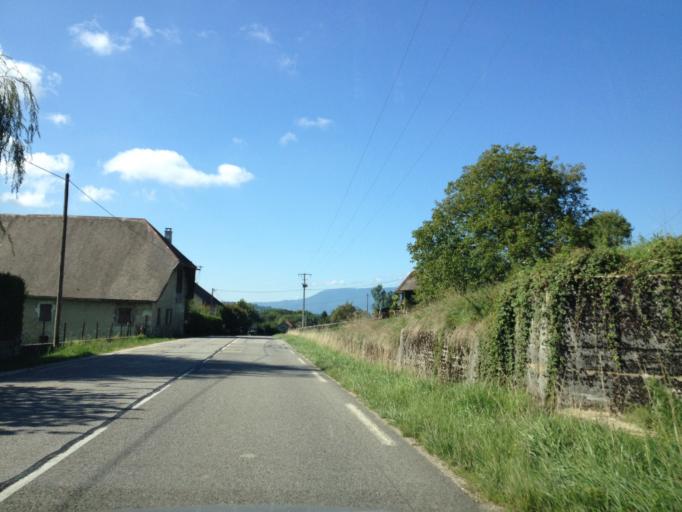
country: FR
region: Rhone-Alpes
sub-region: Departement de la Haute-Savoie
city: Cusy
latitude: 45.7545
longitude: 6.0018
